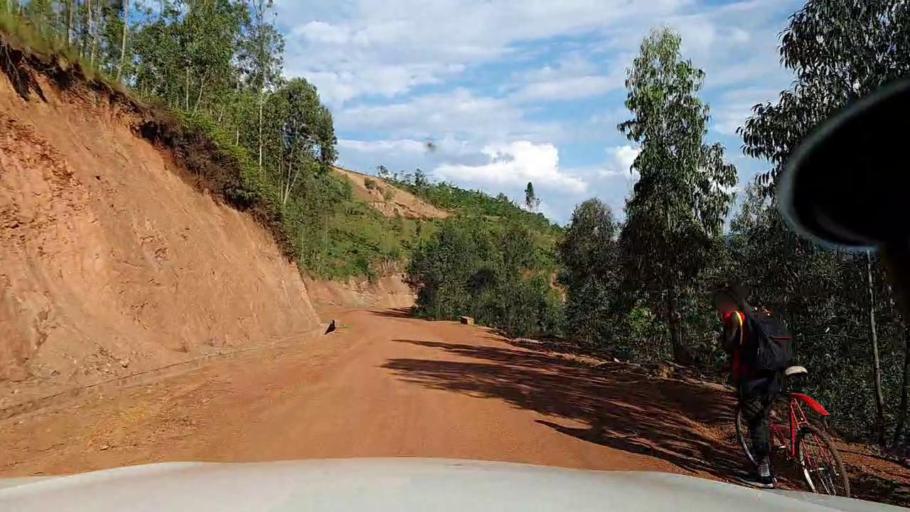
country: RW
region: Kigali
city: Kigali
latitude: -1.8468
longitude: 29.8615
